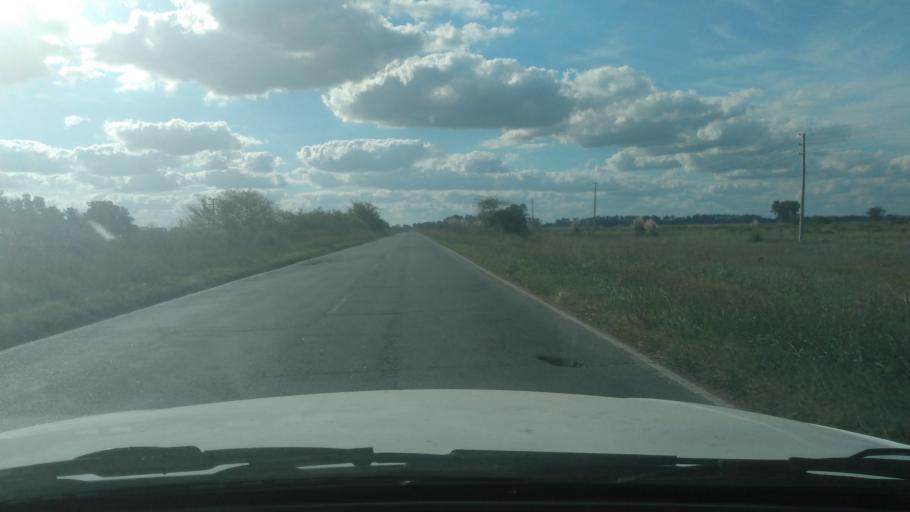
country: AR
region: Buenos Aires
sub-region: Partido de Mercedes
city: Mercedes
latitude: -34.7352
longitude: -59.3880
